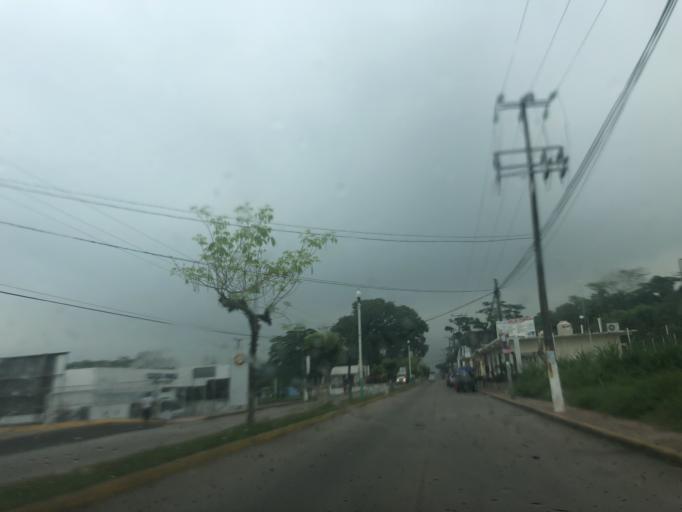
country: MX
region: Chiapas
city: Pichucalco
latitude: 17.5149
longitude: -93.1143
